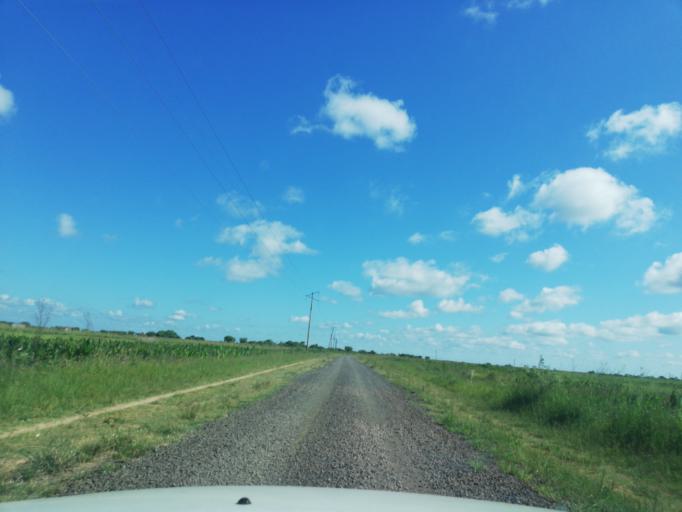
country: AR
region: Corrientes
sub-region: Departamento de San Miguel
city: San Miguel
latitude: -27.9765
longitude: -57.5808
